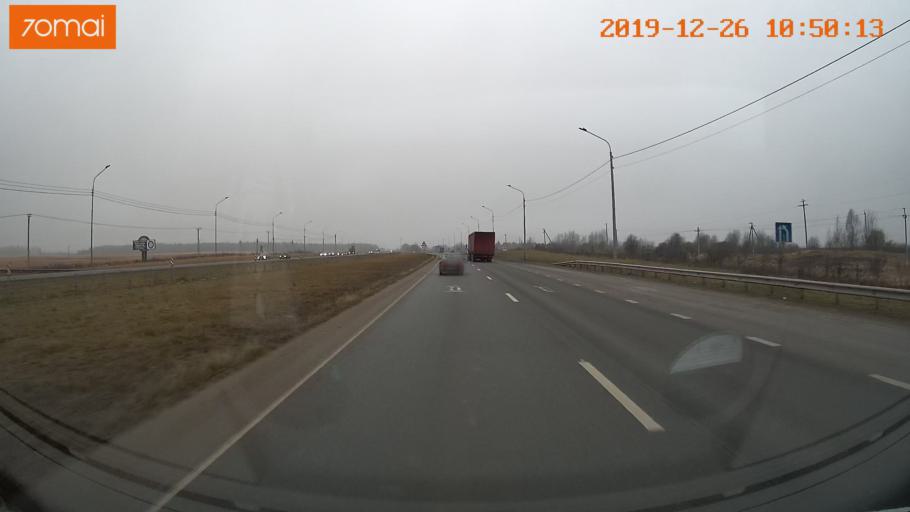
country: RU
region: Vologda
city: Molochnoye
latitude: 59.2100
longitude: 39.6948
